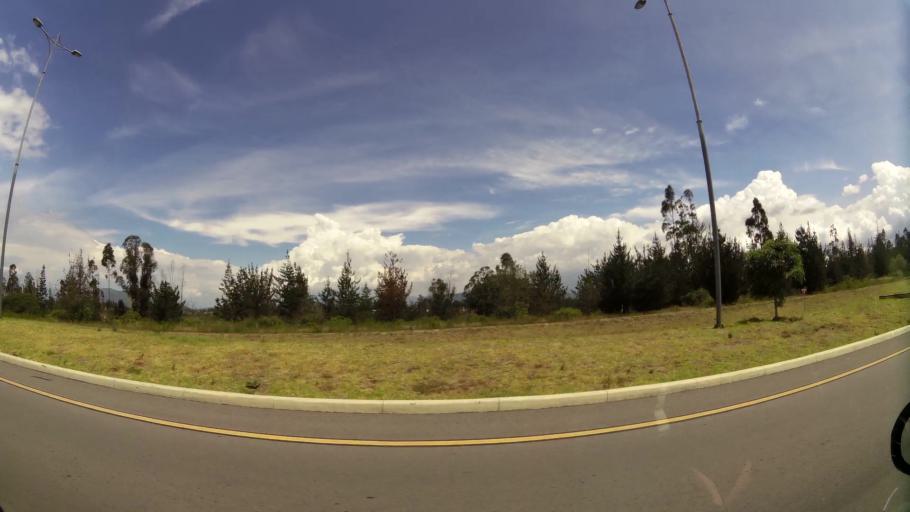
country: EC
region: Pichincha
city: Quito
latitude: -0.1444
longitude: -78.3554
